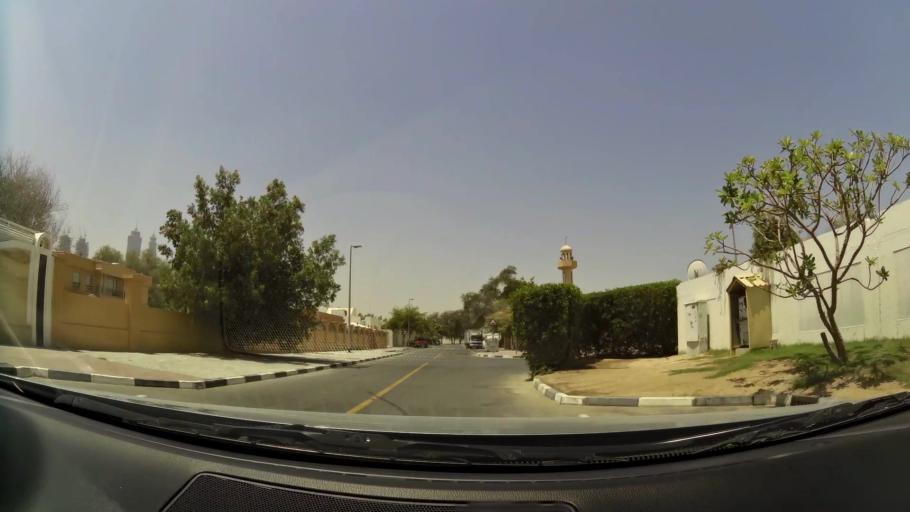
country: AE
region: Dubai
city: Dubai
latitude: 25.2000
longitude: 55.2555
